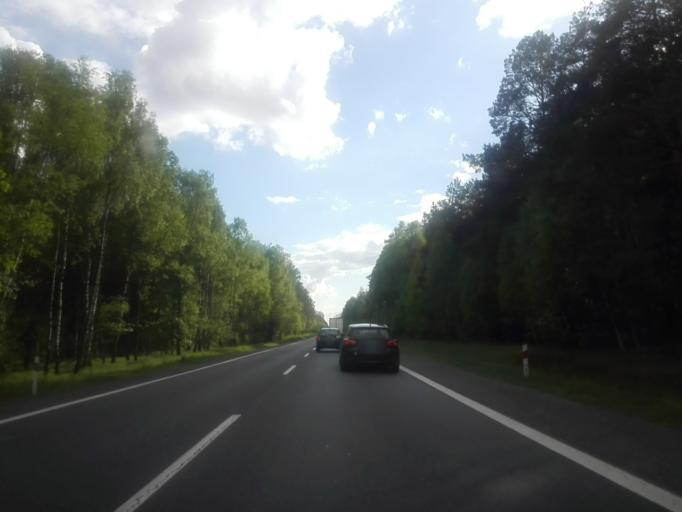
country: PL
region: Masovian Voivodeship
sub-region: Powiat wyszkowski
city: Dlugosiodlo
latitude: 52.7098
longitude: 21.6875
